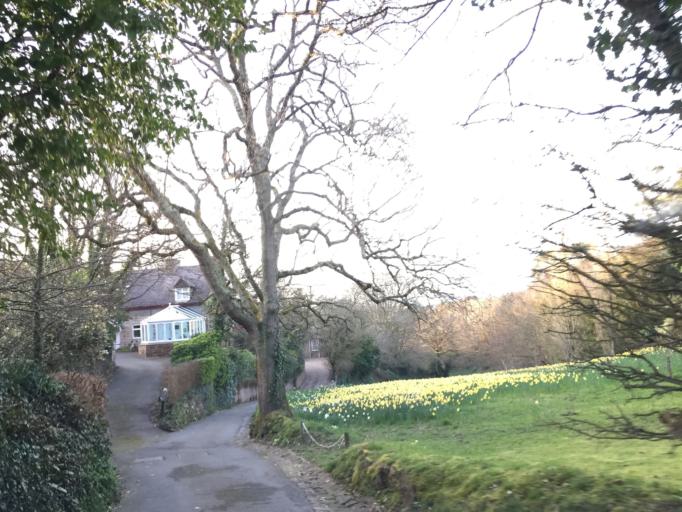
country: JE
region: St Helier
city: Saint Helier
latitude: 49.2303
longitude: -2.0490
